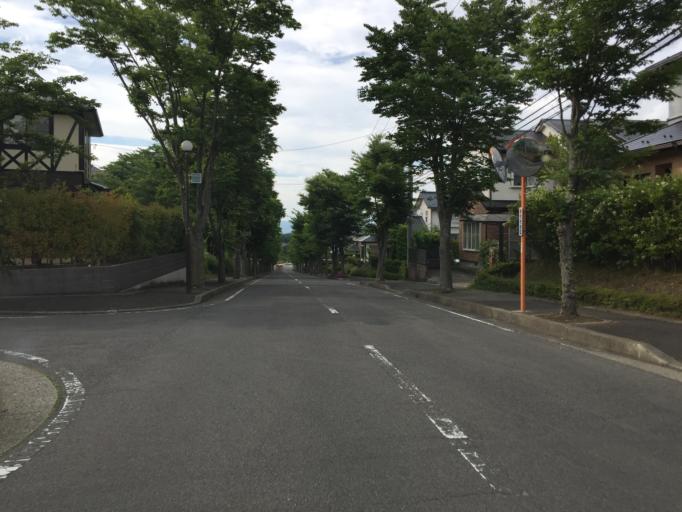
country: JP
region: Fukushima
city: Fukushima-shi
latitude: 37.6628
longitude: 140.4709
